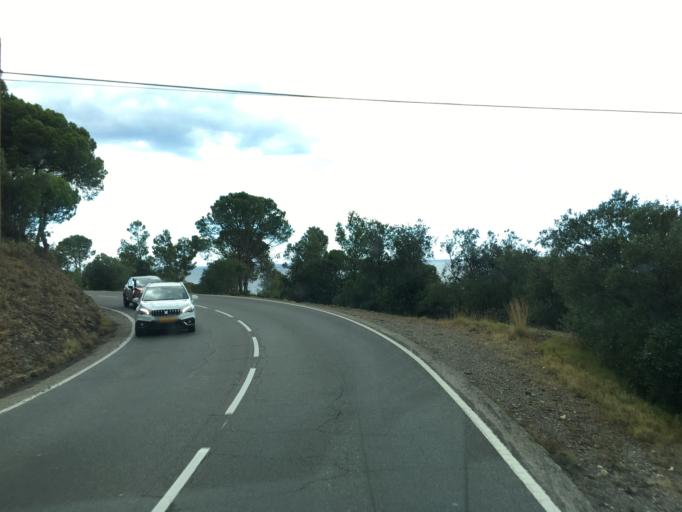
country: ES
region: Catalonia
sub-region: Provincia de Girona
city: Llanca
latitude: 42.3506
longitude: 3.1764
